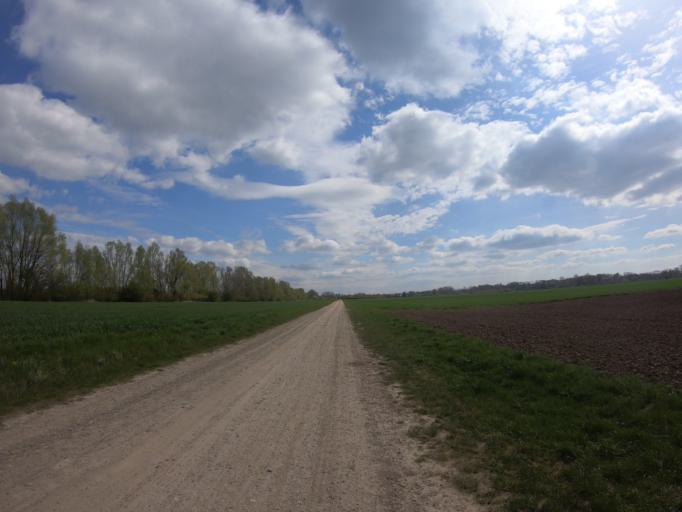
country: DE
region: Lower Saxony
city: Sarstedt
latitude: 52.2575
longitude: 9.8235
